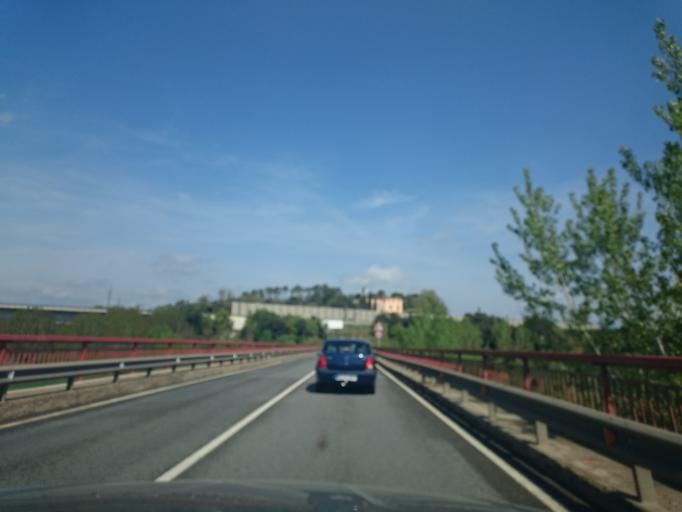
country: ES
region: Catalonia
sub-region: Provincia de Girona
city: Bascara
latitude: 42.1629
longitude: 2.9100
